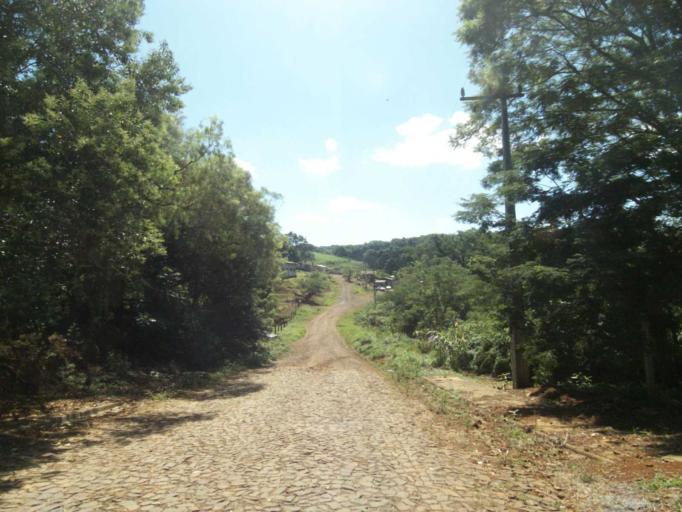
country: BR
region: Parana
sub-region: Laranjeiras Do Sul
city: Laranjeiras do Sul
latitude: -25.3820
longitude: -52.2086
